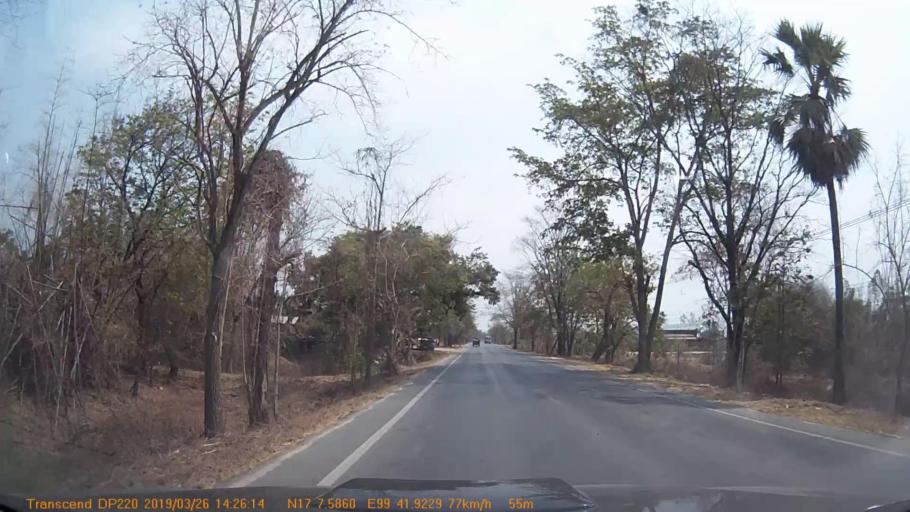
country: TH
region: Sukhothai
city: Ban Na
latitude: 17.1262
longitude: 99.6988
